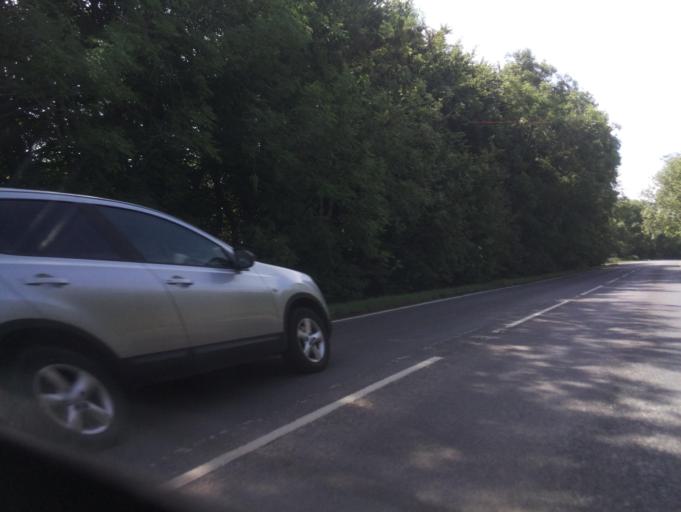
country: GB
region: England
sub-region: North Lincolnshire
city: Manton
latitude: 53.5009
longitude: -0.5824
